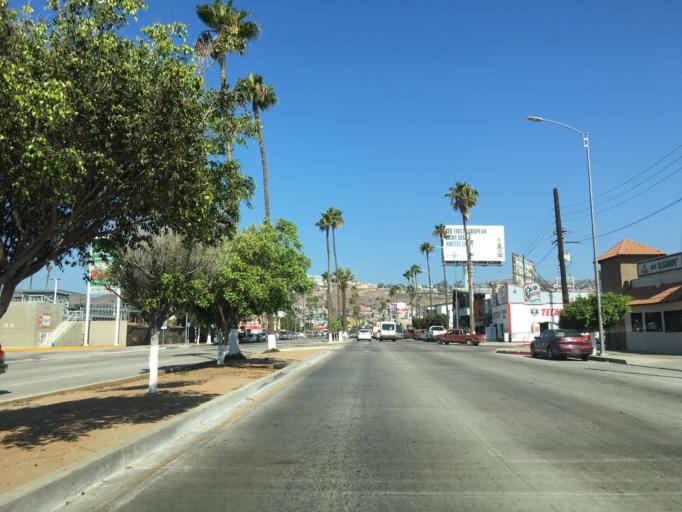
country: MX
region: Baja California
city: Ensenada
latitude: 31.8596
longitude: -116.6219
